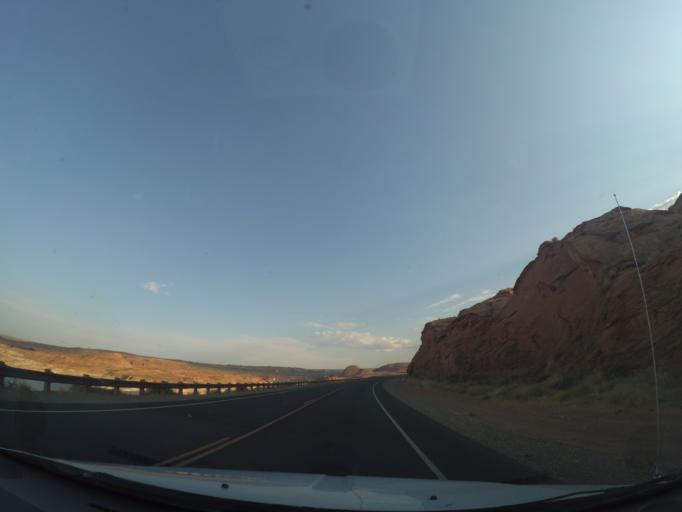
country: US
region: Arizona
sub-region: Coconino County
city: Page
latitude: 36.9550
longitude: -111.4929
